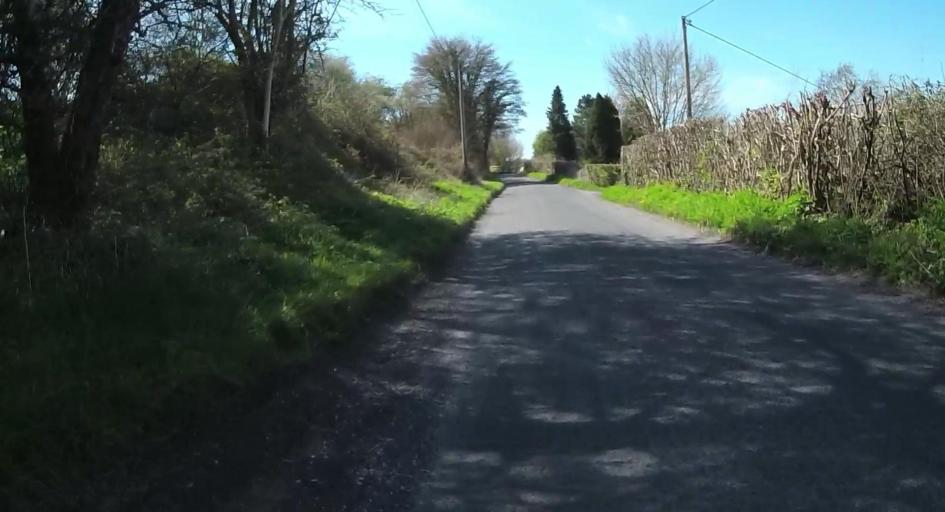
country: GB
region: England
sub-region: Hampshire
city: Romsey
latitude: 51.0716
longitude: -1.5008
